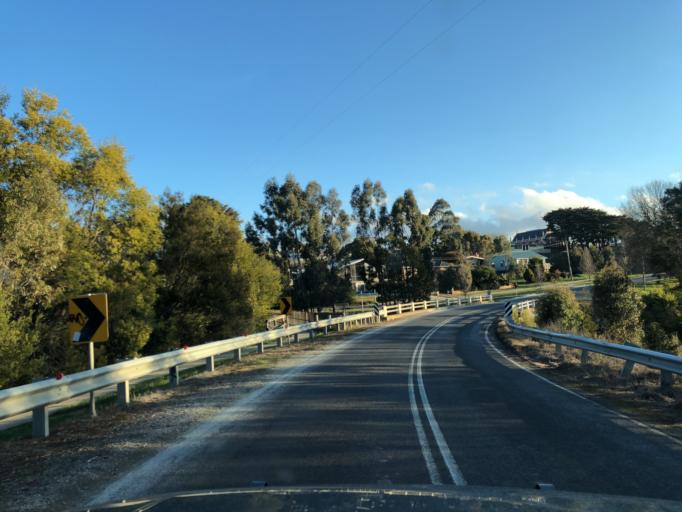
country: AU
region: Victoria
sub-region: Moorabool
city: Bacchus Marsh
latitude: -37.5982
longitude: 144.2310
